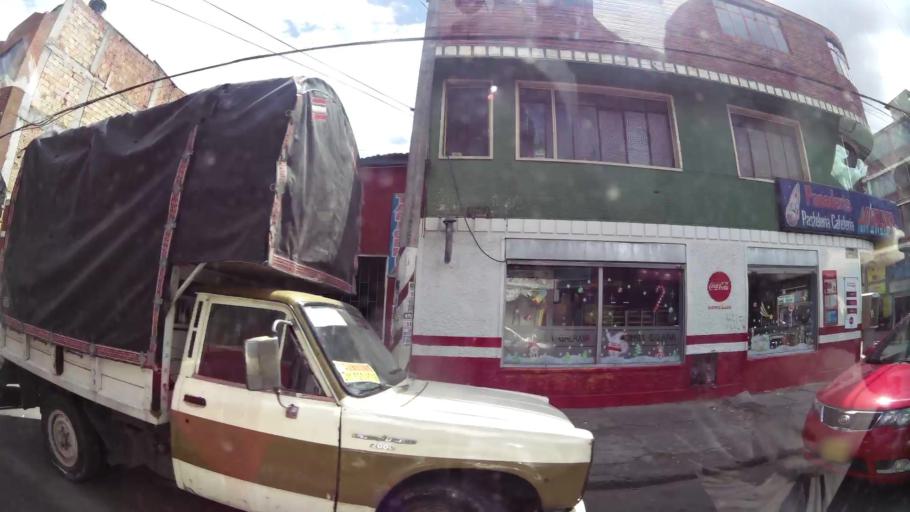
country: CO
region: Bogota D.C.
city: Bogota
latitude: 4.6051
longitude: -74.1276
